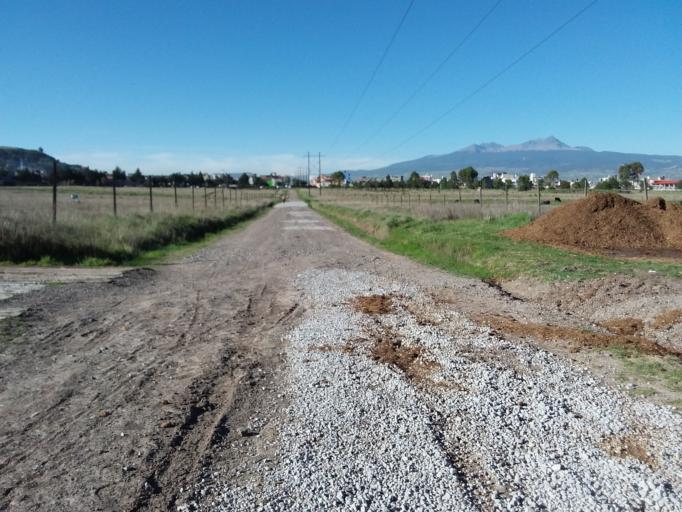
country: MX
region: Mexico
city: San Marcos Yachihuacaltepec
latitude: 19.3093
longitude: -99.6955
